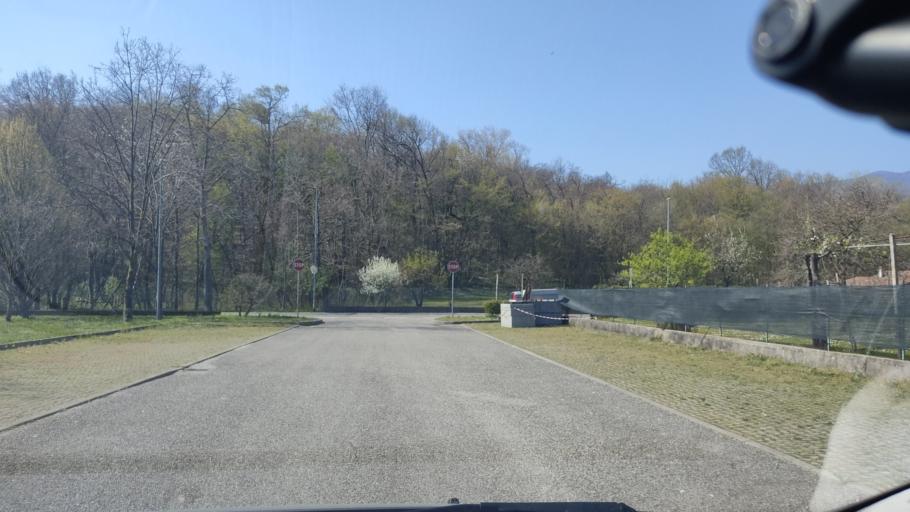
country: IT
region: Friuli Venezia Giulia
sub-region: Provincia di Pordenone
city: Budoia
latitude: 46.0410
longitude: 12.5333
